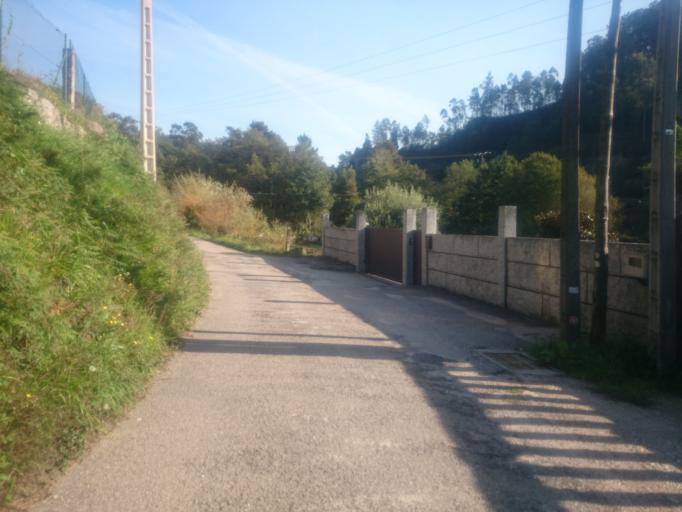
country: ES
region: Galicia
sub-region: Provincia de Pontevedra
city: Porrino
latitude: 42.1574
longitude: -8.6059
